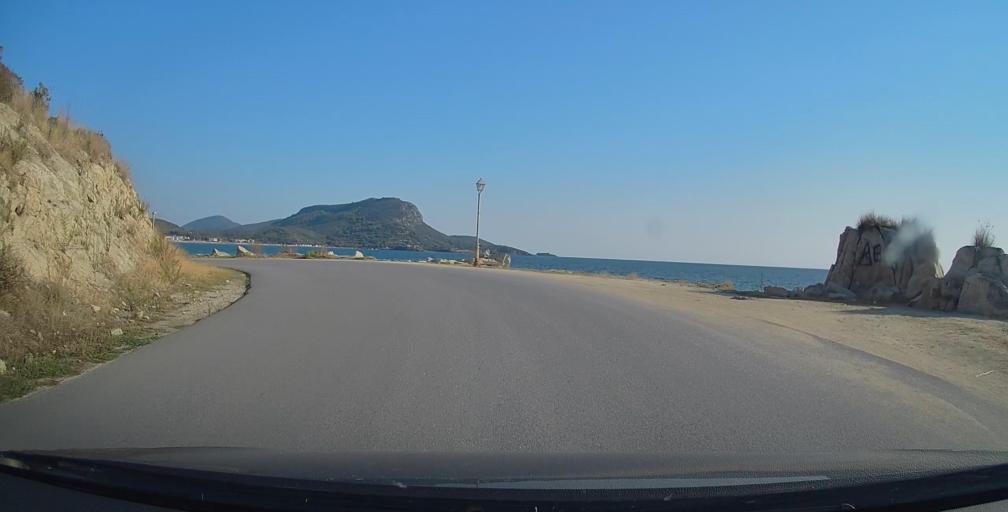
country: GR
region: Central Macedonia
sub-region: Nomos Chalkidikis
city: Sykia
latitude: 39.9907
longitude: 23.8938
